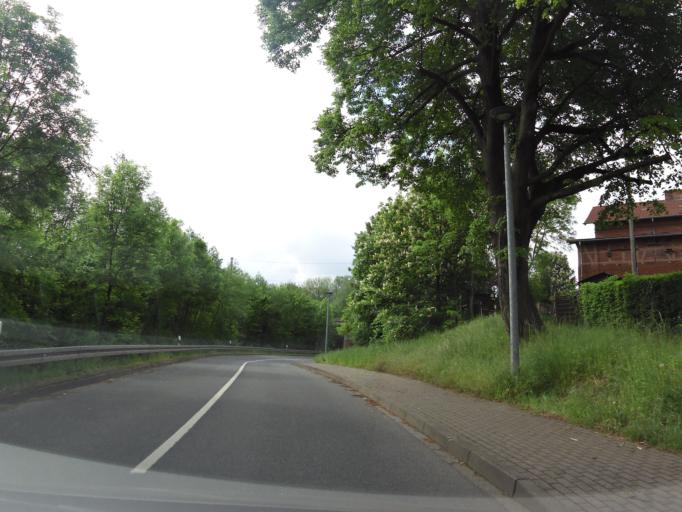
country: DE
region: Thuringia
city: Horselgau
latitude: 50.9311
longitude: 10.5741
